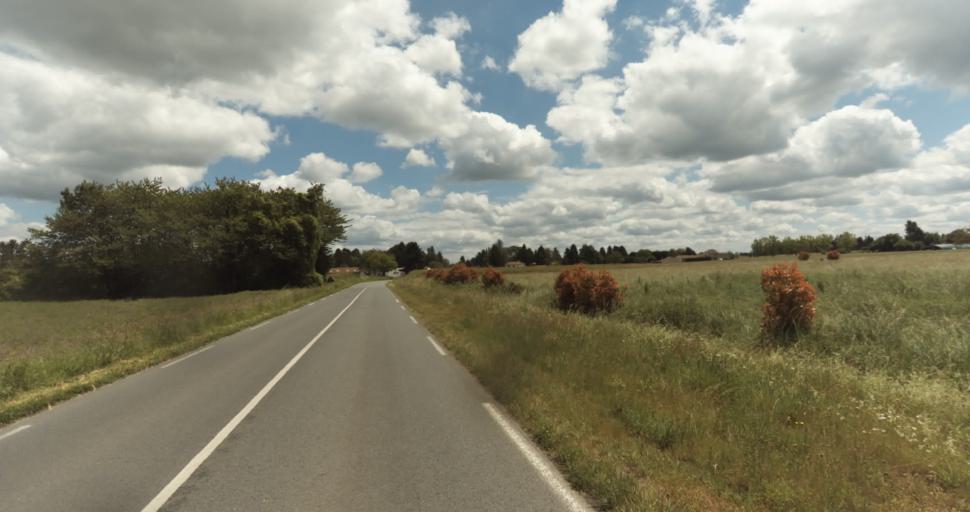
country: FR
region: Aquitaine
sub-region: Departement de la Dordogne
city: Beaumont-du-Perigord
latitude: 44.6904
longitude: 0.8809
